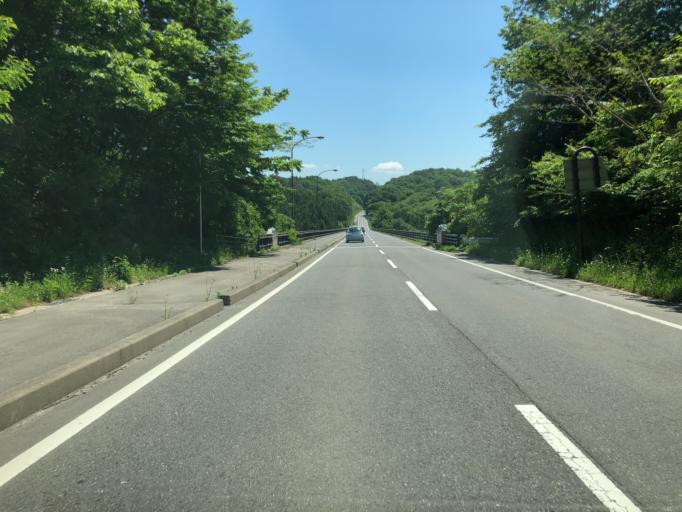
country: JP
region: Fukushima
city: Motomiya
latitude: 37.5360
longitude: 140.4135
